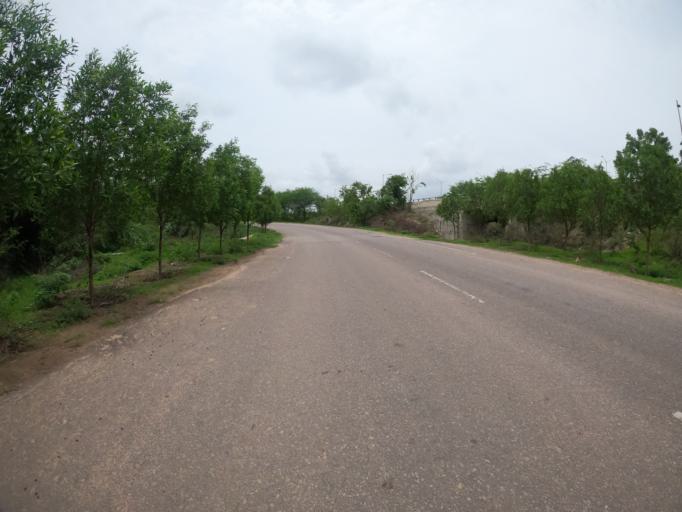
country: IN
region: Telangana
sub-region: Hyderabad
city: Hyderabad
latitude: 17.3473
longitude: 78.3604
